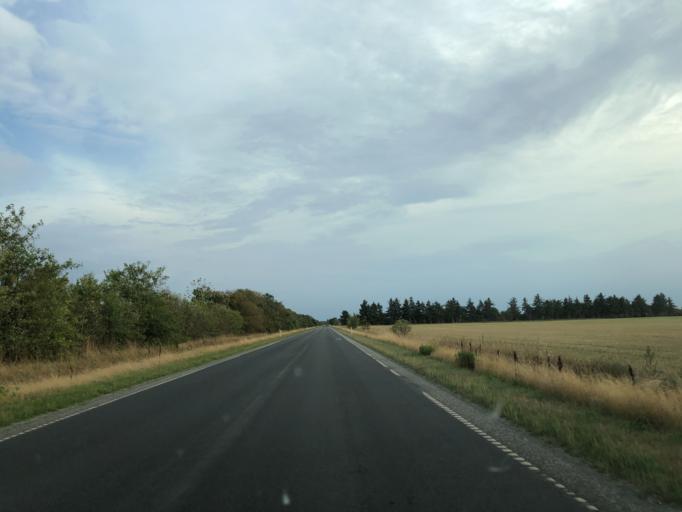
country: DK
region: Central Jutland
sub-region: Holstebro Kommune
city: Holstebro
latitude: 56.3892
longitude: 8.4548
